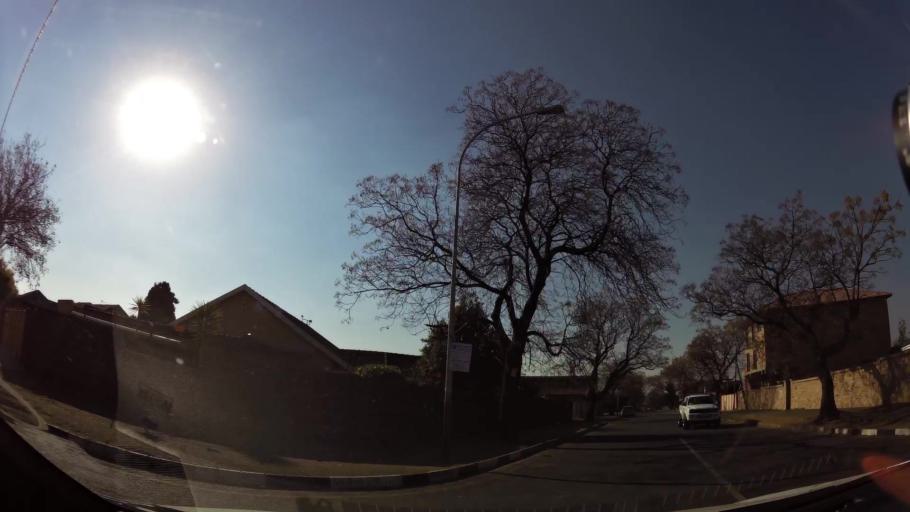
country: ZA
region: Gauteng
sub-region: City of Johannesburg Metropolitan Municipality
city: Johannesburg
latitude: -26.2538
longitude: 28.0115
